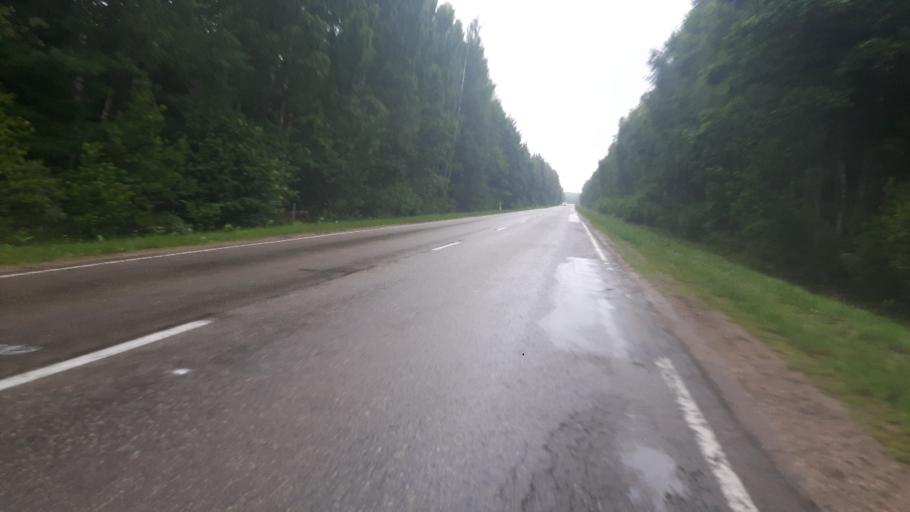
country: LV
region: Rucavas
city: Rucava
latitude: 56.1242
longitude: 21.1465
